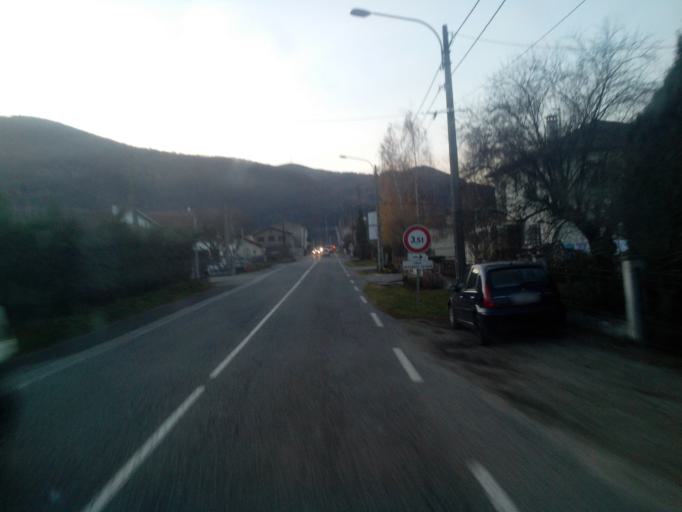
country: FR
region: Midi-Pyrenees
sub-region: Departement de l'Ariege
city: Saint-Paul-de-Jarrat
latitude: 42.9176
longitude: 1.6434
